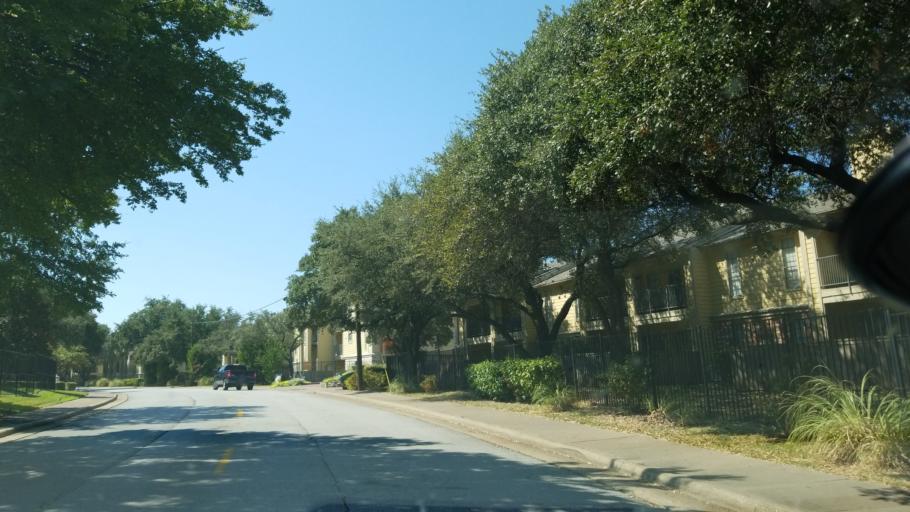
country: US
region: Texas
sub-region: Dallas County
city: Richardson
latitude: 32.9069
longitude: -96.7131
